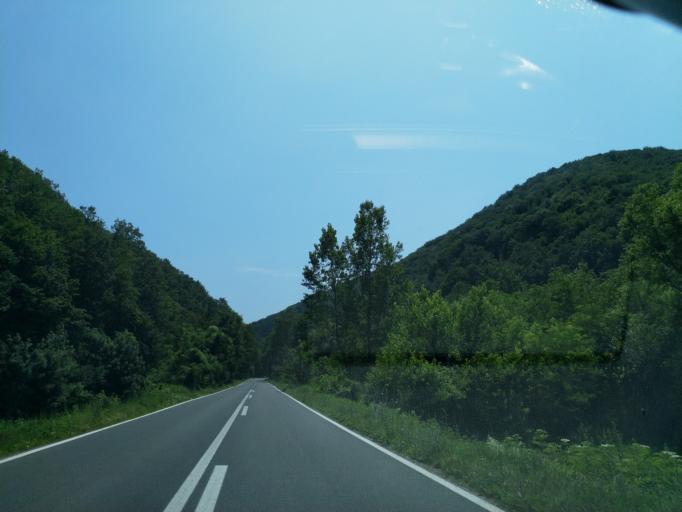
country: RS
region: Central Serbia
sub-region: Toplicki Okrug
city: Blace
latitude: 43.3396
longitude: 21.2040
